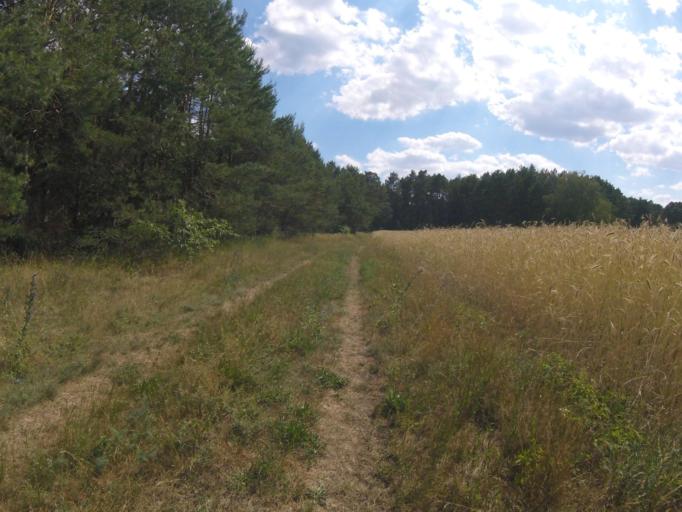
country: DE
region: Brandenburg
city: Wildau
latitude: 52.3322
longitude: 13.6764
